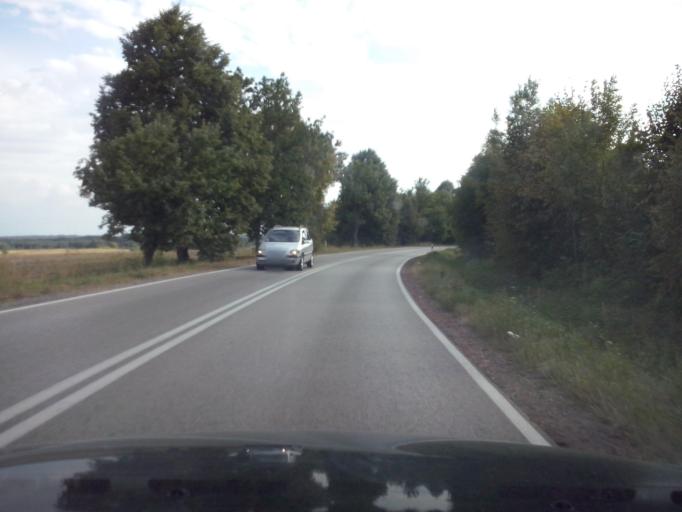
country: PL
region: Swietokrzyskie
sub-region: Powiat kielecki
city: Rakow
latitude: 50.6904
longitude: 21.0593
